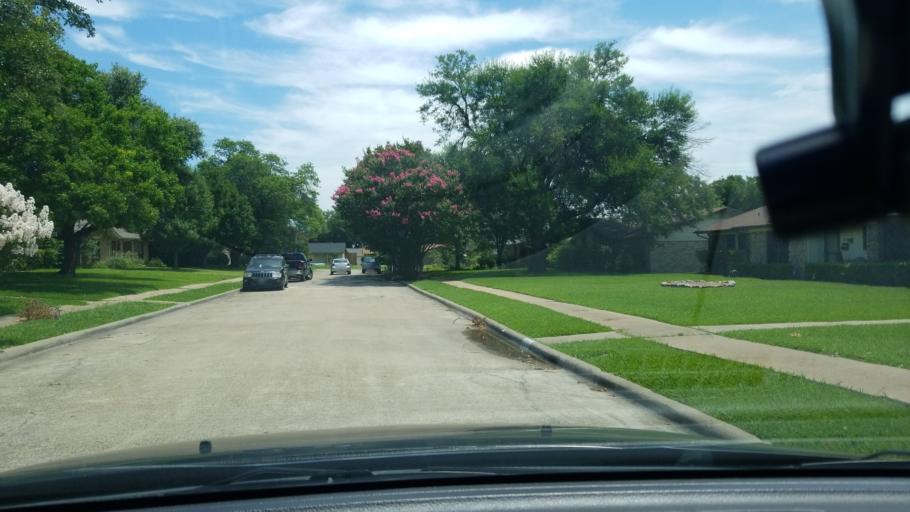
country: US
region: Texas
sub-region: Dallas County
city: Mesquite
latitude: 32.8094
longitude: -96.6500
